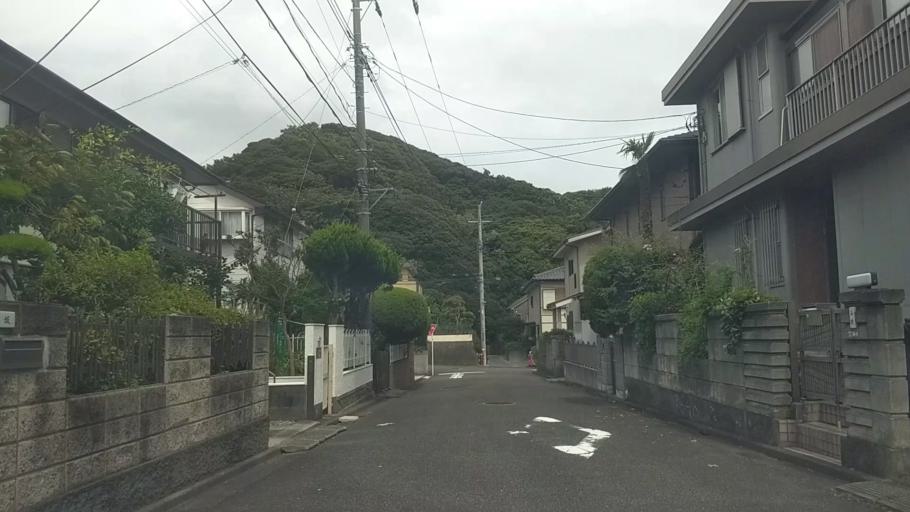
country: JP
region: Kanagawa
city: Yokosuka
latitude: 35.2434
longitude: 139.7251
